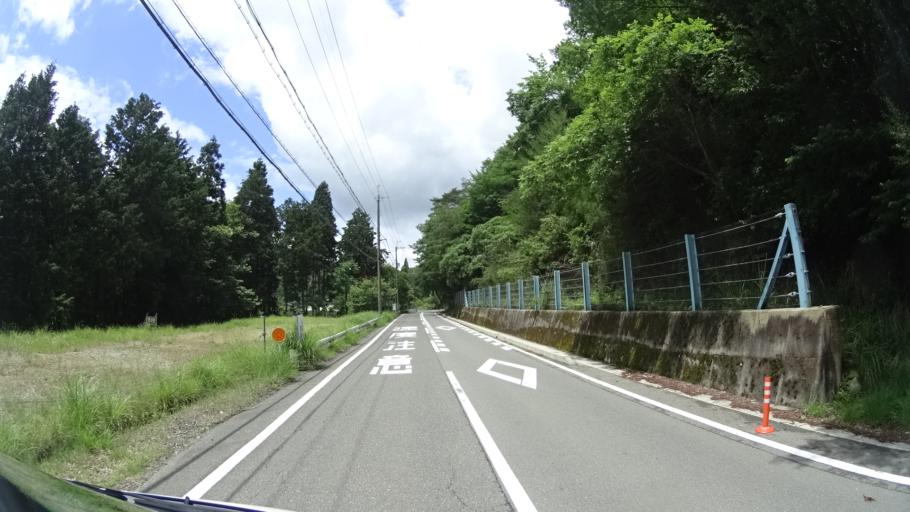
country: JP
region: Kyoto
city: Kameoka
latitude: 35.0216
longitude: 135.4011
